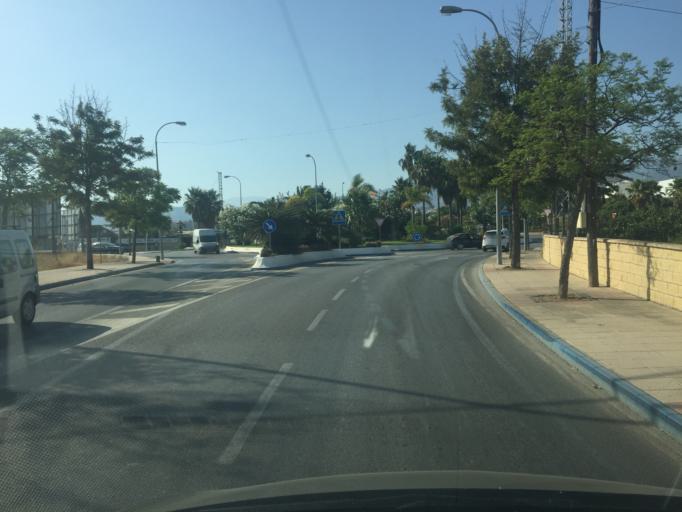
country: ES
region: Andalusia
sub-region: Provincia de Malaga
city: Nerja
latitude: 36.7486
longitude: -3.8824
